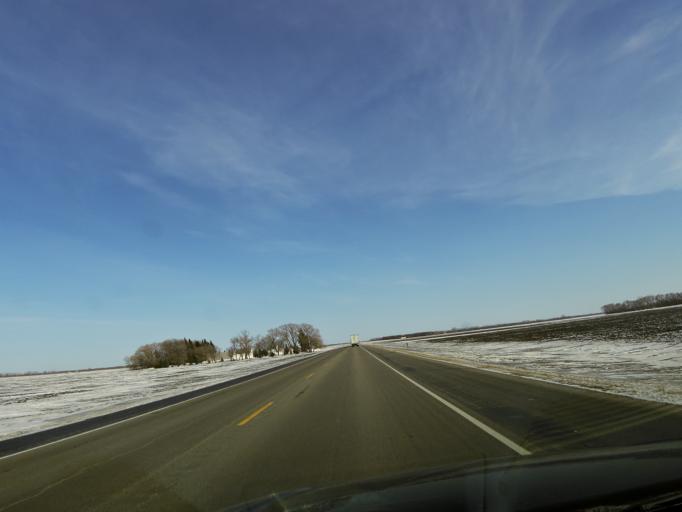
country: US
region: North Dakota
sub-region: Walsh County
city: Grafton
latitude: 48.4121
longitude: -97.2117
